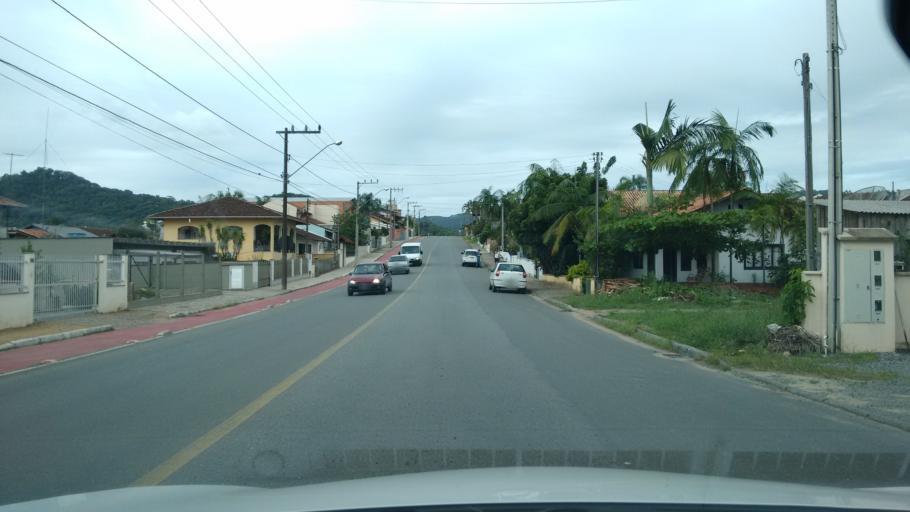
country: BR
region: Santa Catarina
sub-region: Timbo
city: Timbo
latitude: -26.8115
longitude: -49.2700
